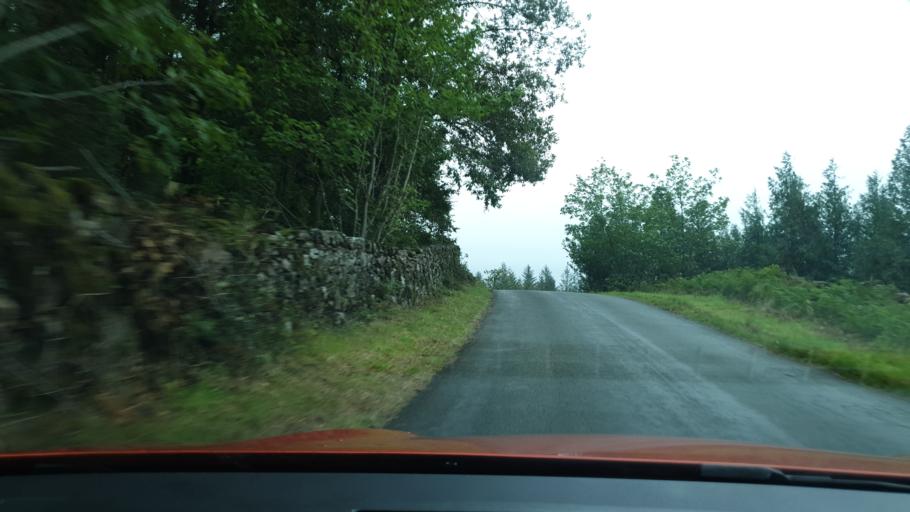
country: GB
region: England
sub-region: Cumbria
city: Seascale
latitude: 54.3985
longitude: -3.3567
